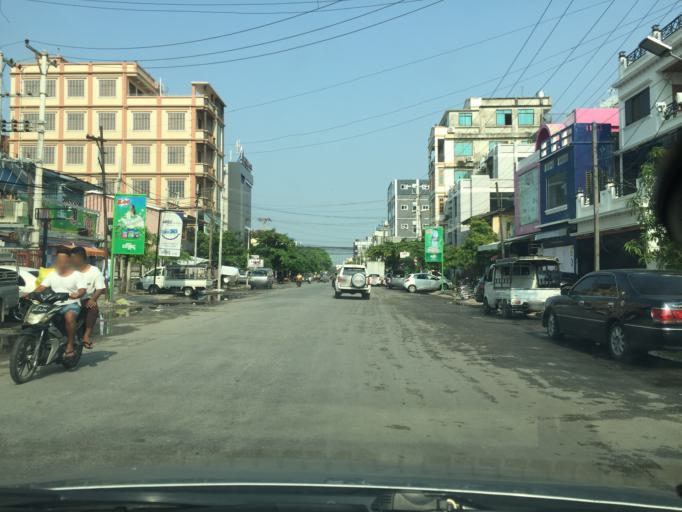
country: MM
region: Mandalay
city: Mandalay
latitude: 21.9725
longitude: 96.0831
